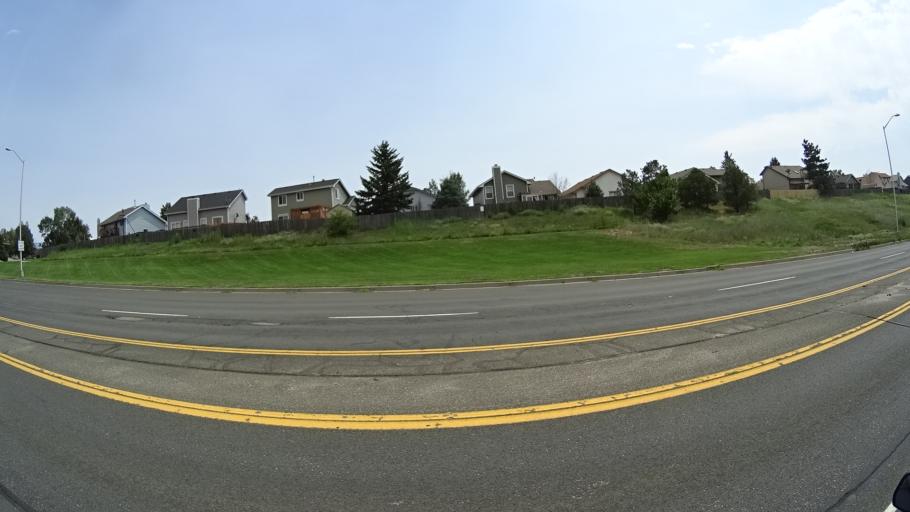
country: US
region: Colorado
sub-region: El Paso County
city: Black Forest
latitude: 38.9517
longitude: -104.7401
